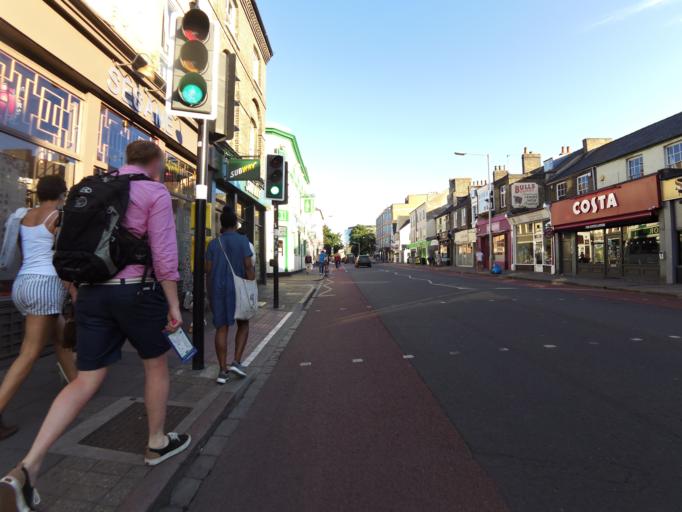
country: GB
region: England
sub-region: Cambridgeshire
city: Cambridge
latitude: 52.1973
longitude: 0.1292
